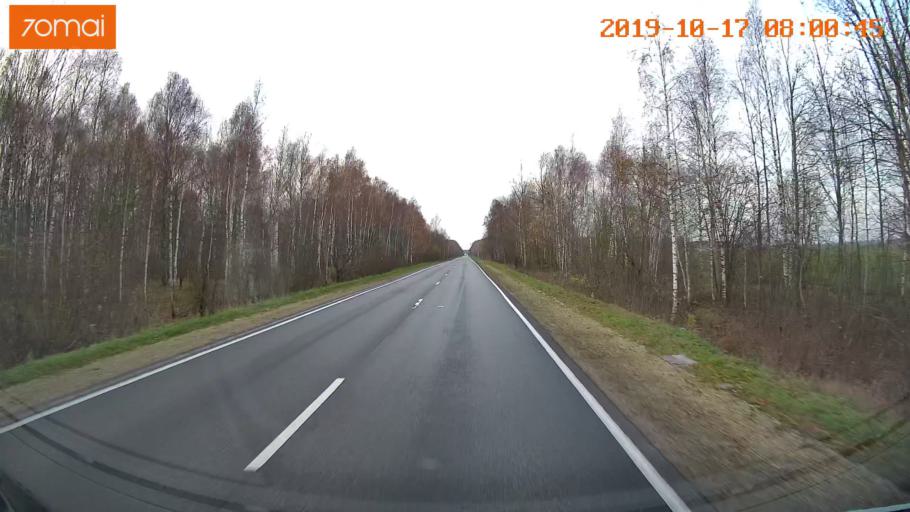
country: RU
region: Vladimir
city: Bavleny
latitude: 56.3801
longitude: 39.5112
